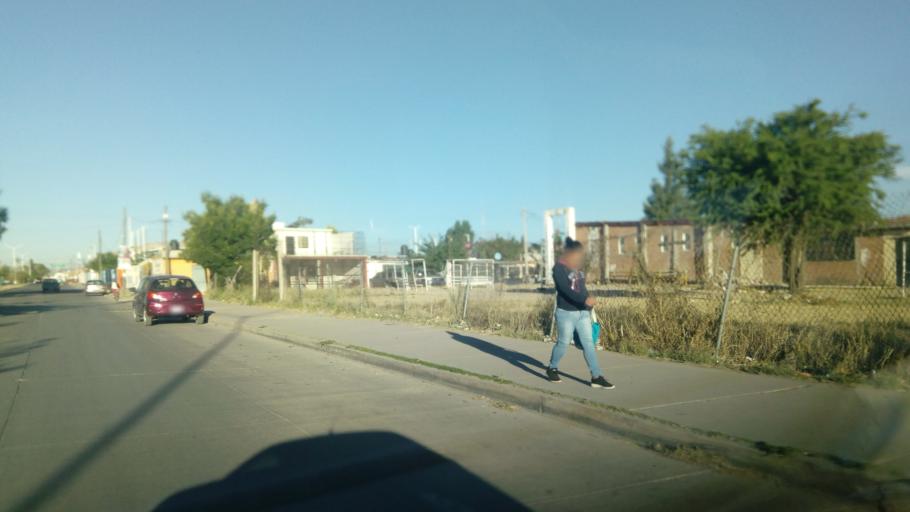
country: MX
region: Durango
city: Victoria de Durango
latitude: 24.0554
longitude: -104.5943
